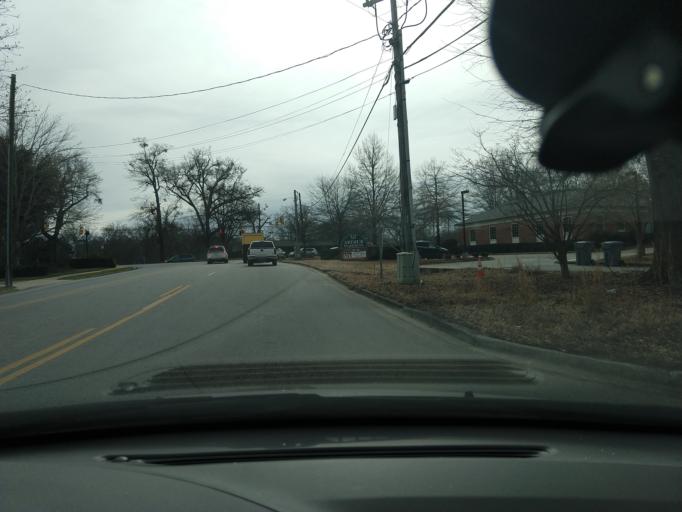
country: US
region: South Carolina
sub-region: Spartanburg County
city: Spartanburg
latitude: 34.9577
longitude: -81.9120
